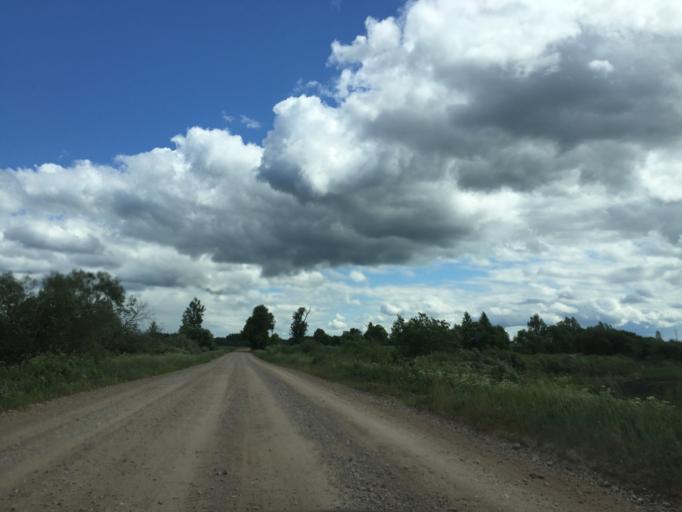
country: LV
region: Lecava
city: Iecava
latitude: 56.5051
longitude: 24.3537
